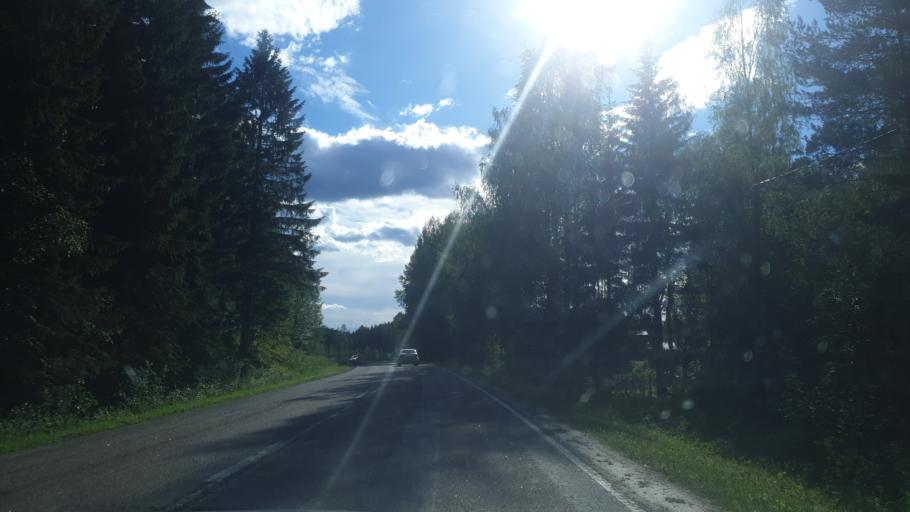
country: FI
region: Southern Savonia
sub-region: Mikkeli
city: Pertunmaa
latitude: 61.5254
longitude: 26.6010
